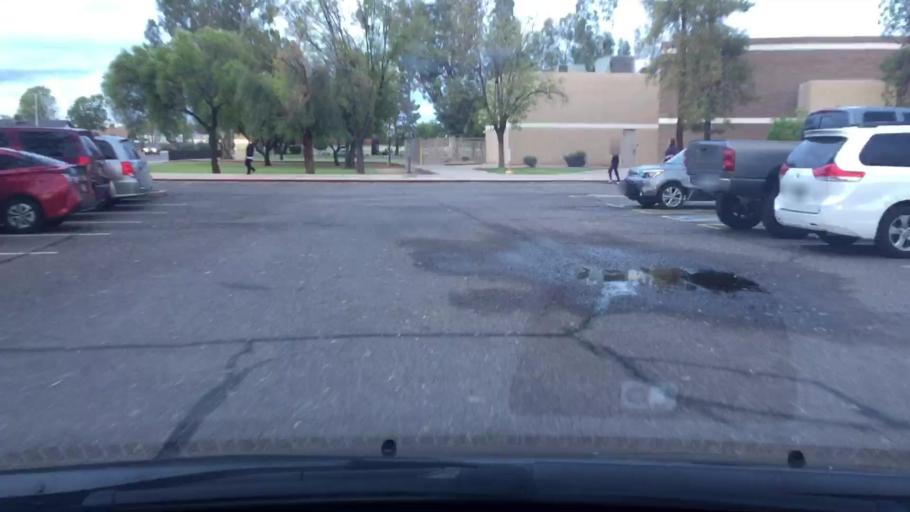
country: US
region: Arizona
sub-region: Maricopa County
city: Gilbert
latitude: 33.4032
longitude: -111.7622
